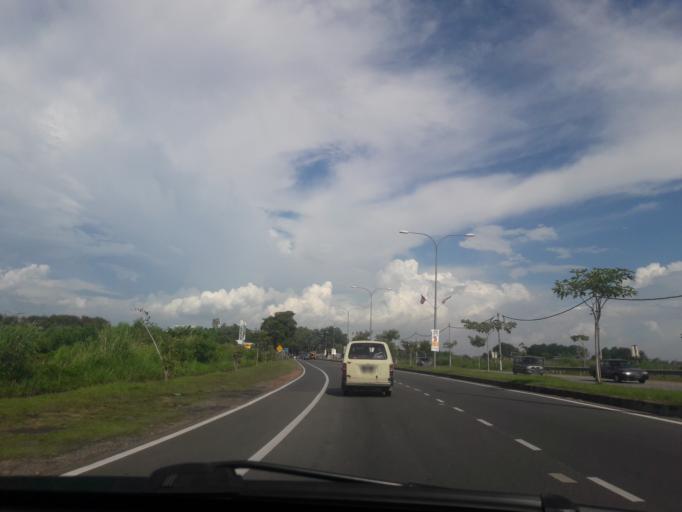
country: MY
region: Kedah
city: Sungai Petani
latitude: 5.6160
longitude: 100.4686
